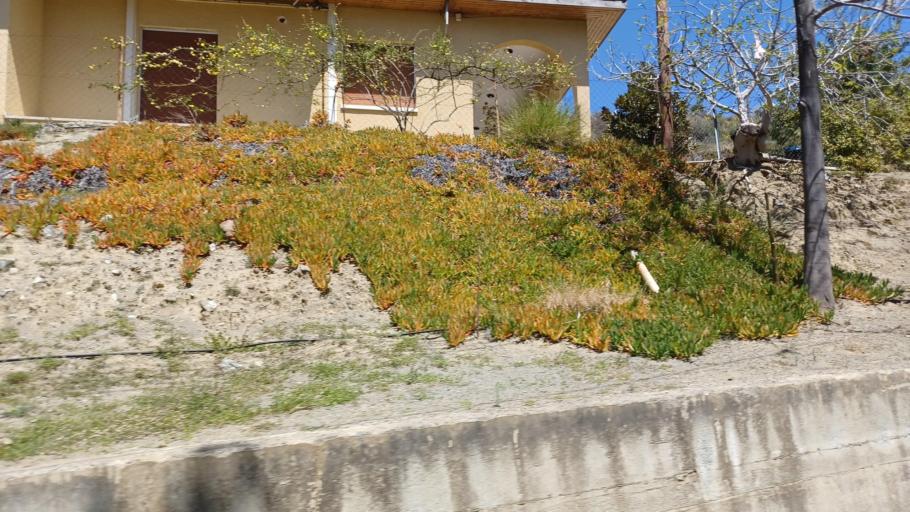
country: CY
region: Limassol
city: Parekklisha
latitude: 34.8127
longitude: 33.1461
